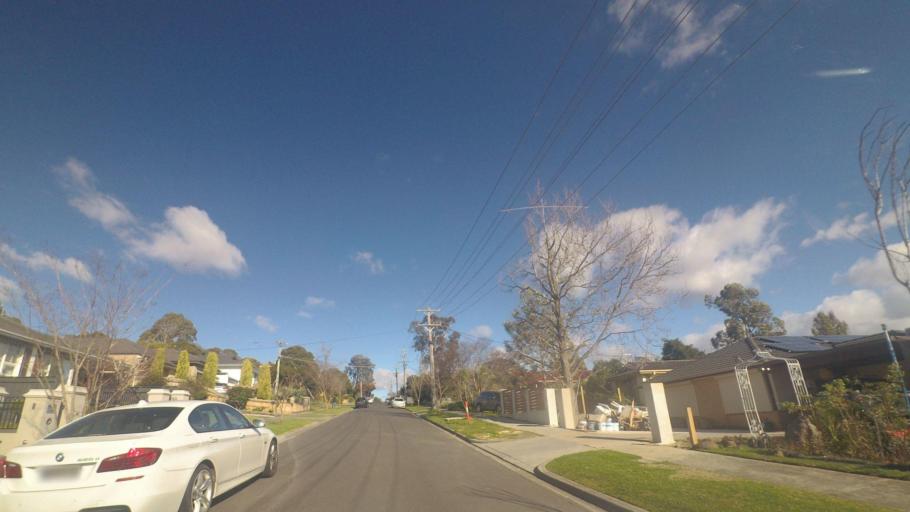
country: AU
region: Victoria
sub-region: Boroondara
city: Balwyn North
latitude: -37.7825
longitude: 145.0926
